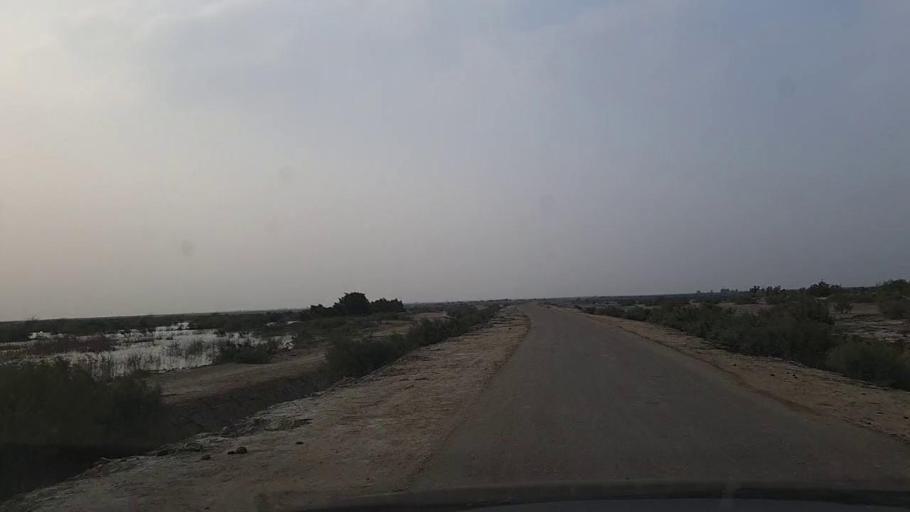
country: PK
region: Sindh
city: Gharo
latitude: 24.7679
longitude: 67.7468
